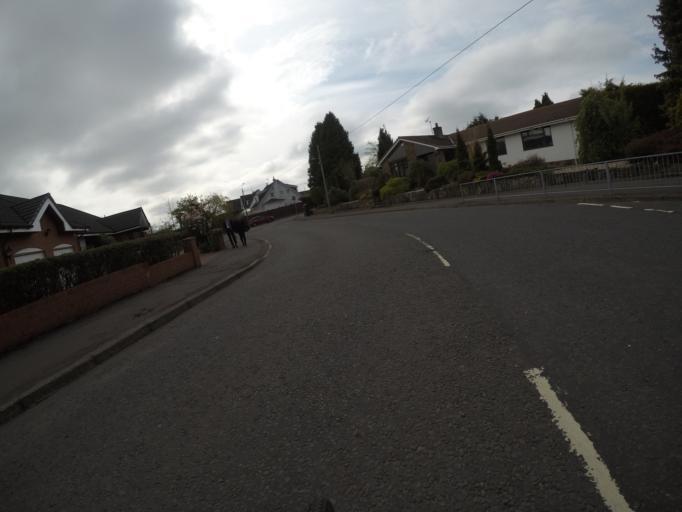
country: GB
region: Scotland
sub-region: East Renfrewshire
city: Newton Mearns
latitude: 55.7772
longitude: -4.3055
